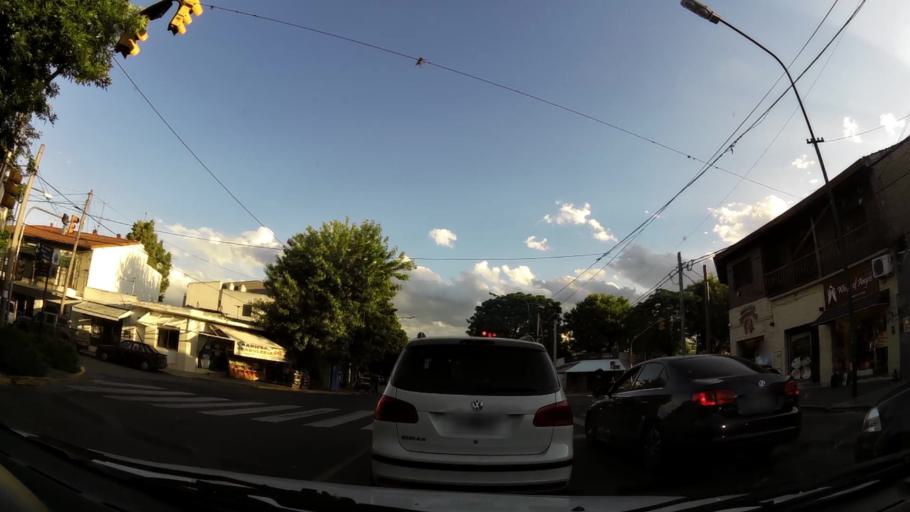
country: AR
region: Buenos Aires
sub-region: Partido de San Isidro
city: San Isidro
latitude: -34.4773
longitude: -58.5298
